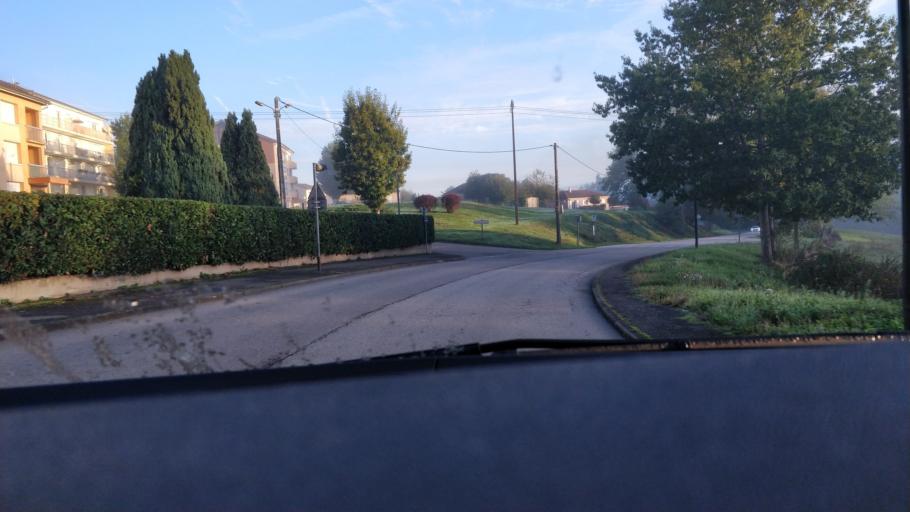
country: FR
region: Limousin
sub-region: Departement de la Haute-Vienne
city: Saint-Leonard-de-Noblat
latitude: 45.8442
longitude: 1.4924
